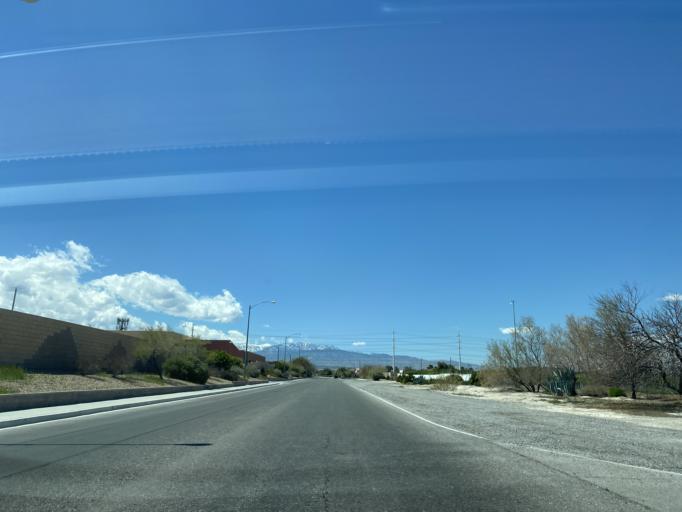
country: US
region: Nevada
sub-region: Clark County
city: North Las Vegas
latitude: 36.3134
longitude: -115.2032
